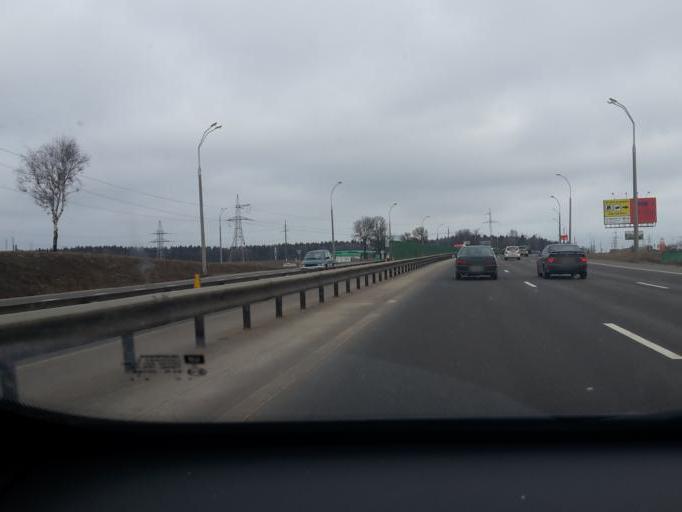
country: BY
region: Minsk
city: Novoye Medvezhino
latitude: 53.9004
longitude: 27.4078
